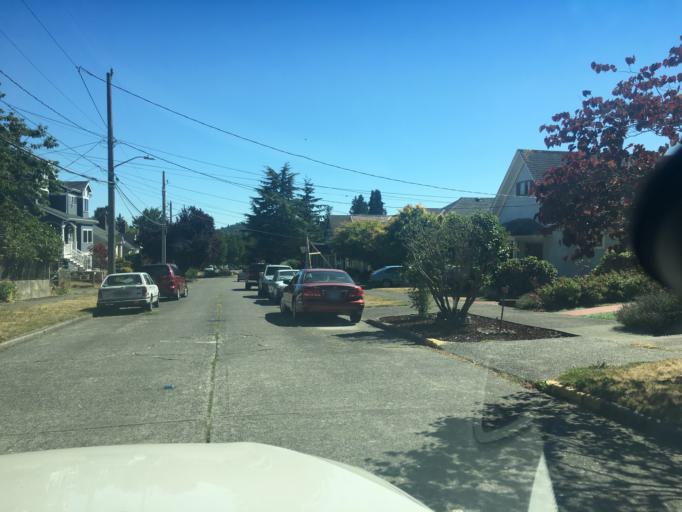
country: US
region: Washington
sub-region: King County
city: Shoreline
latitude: 47.6787
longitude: -122.3898
